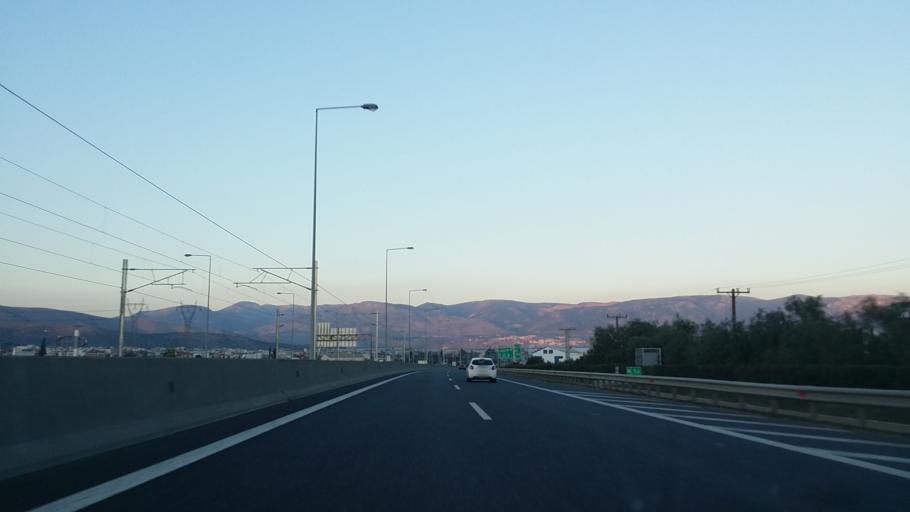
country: GR
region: Attica
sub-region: Nomarchia Dytikis Attikis
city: Magoula
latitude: 38.0648
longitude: 23.5224
